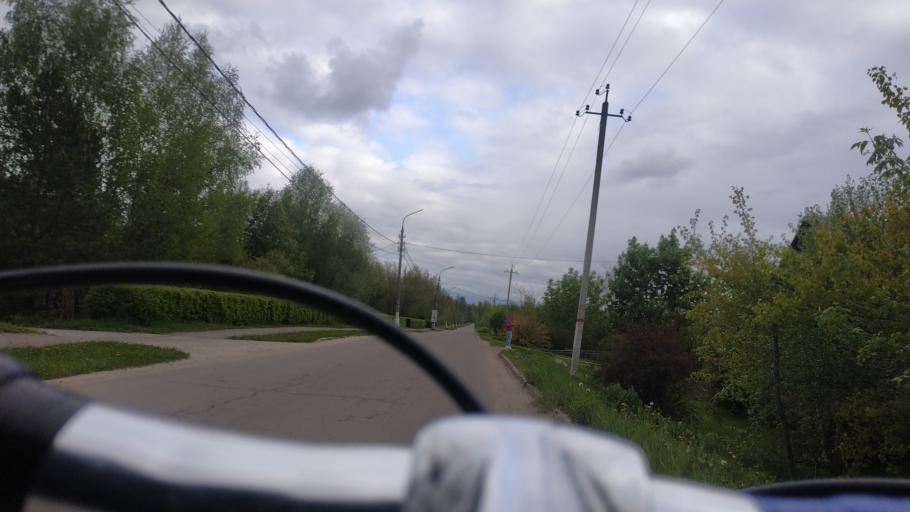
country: RU
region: Moskovskaya
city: Rechitsy
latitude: 55.6111
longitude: 38.5387
